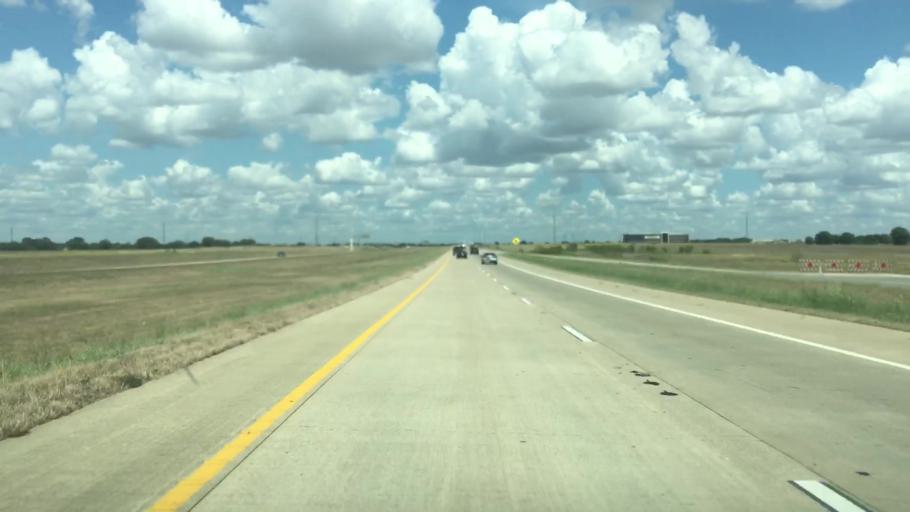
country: US
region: Texas
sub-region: Williamson County
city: Hutto
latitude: 30.5422
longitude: -97.5763
